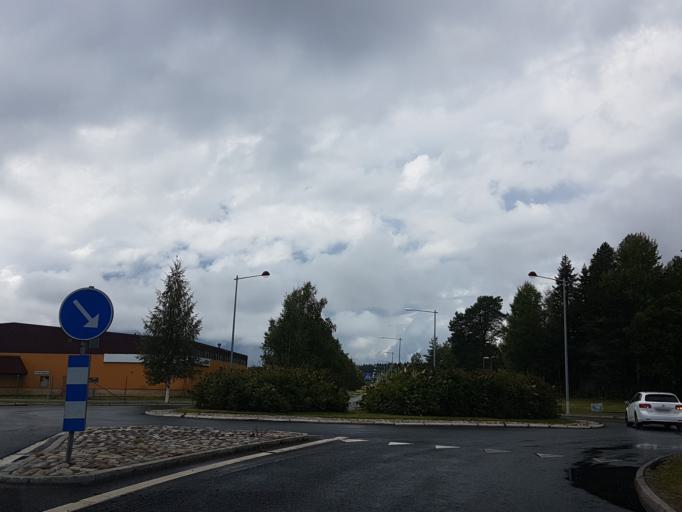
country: SE
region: Vaesterbotten
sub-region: Umea Kommun
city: Ersmark
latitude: 63.8521
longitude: 20.3162
